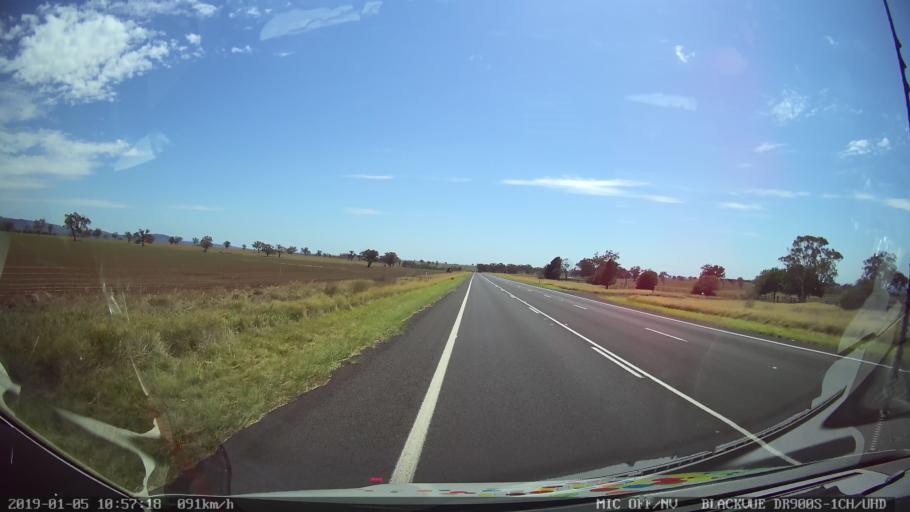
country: AU
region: New South Wales
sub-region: Warrumbungle Shire
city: Coonabarabran
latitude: -31.4325
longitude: 149.1677
